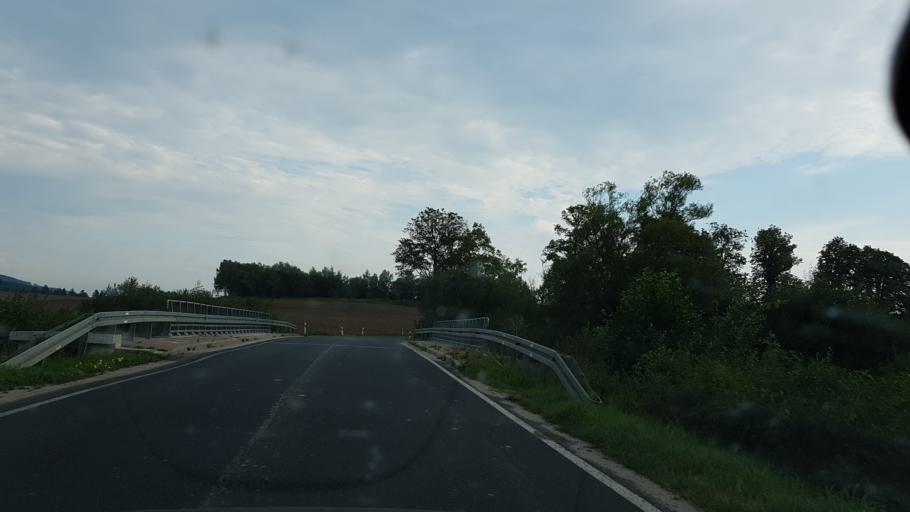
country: PL
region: Lower Silesian Voivodeship
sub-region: Powiat kamiennogorski
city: Marciszow
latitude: 50.8731
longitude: 16.0012
